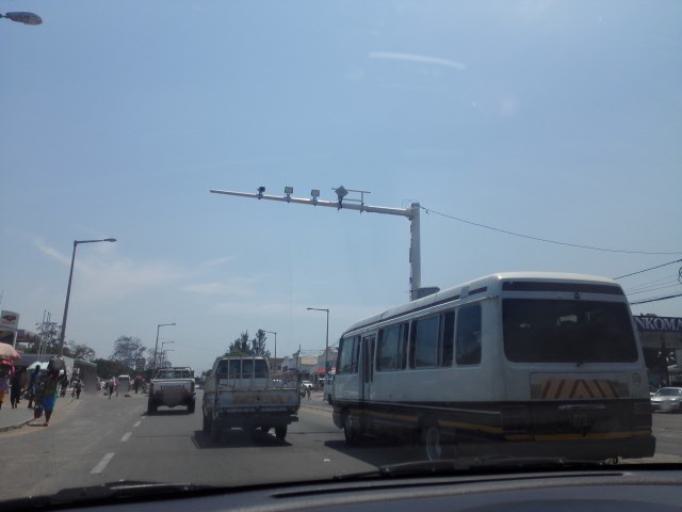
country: MZ
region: Maputo City
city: Maputo
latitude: -25.9274
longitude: 32.5570
